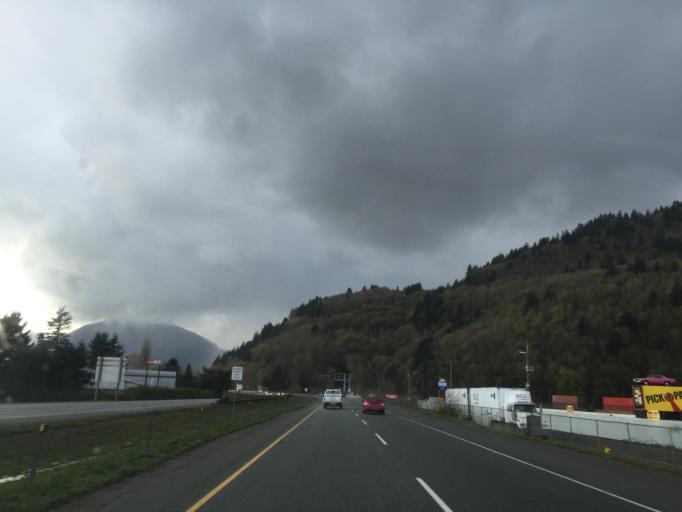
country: CA
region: British Columbia
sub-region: Fraser Valley Regional District
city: Chilliwack
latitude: 49.1445
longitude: -122.0153
